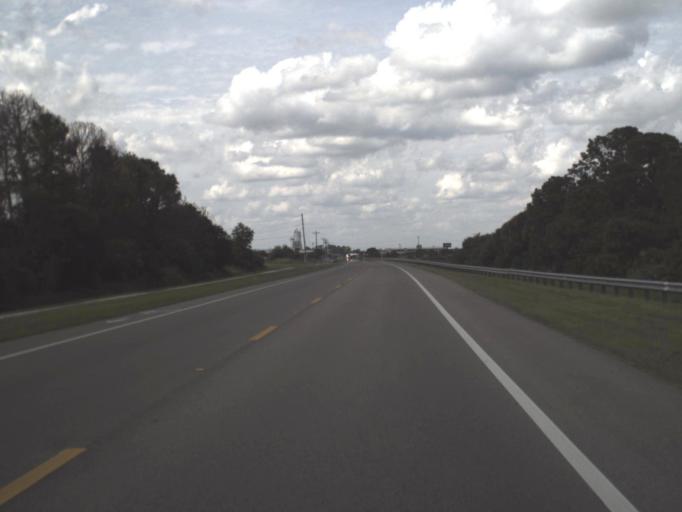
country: US
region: Florida
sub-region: Collier County
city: Immokalee
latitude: 26.4100
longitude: -81.3992
